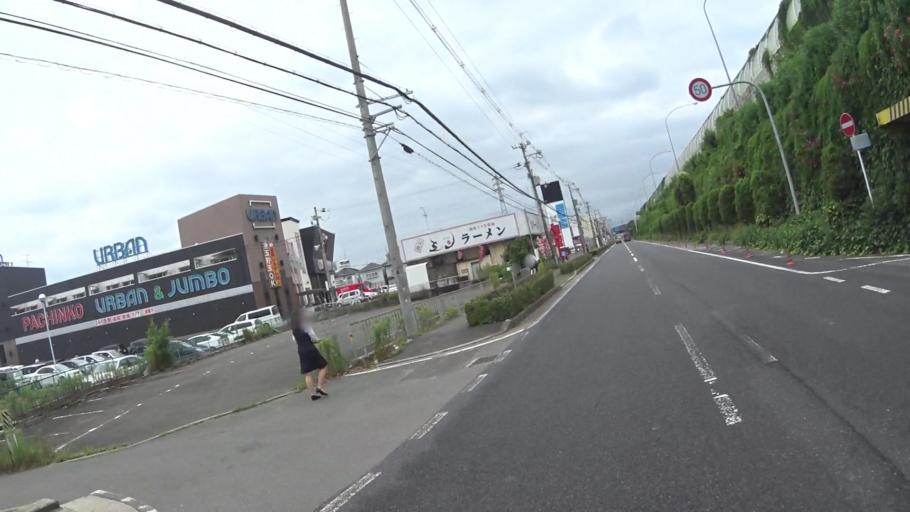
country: JP
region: Kyoto
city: Muko
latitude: 34.9280
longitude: 135.7121
